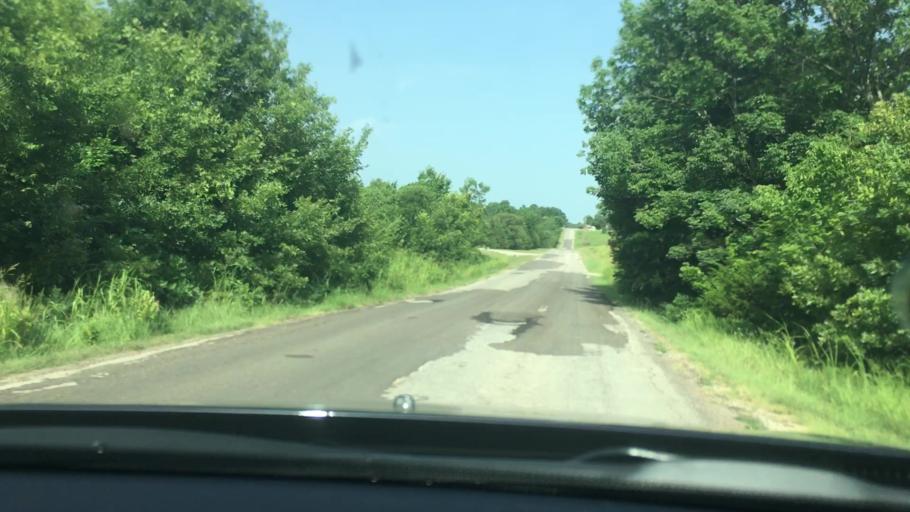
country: US
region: Oklahoma
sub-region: Pontotoc County
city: Byng
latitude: 34.8737
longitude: -96.5818
